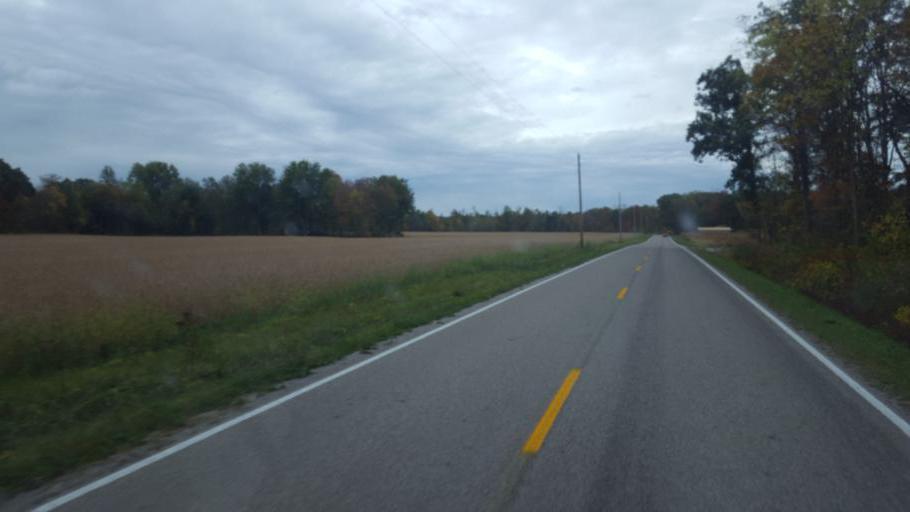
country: US
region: Ohio
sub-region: Huron County
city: New London
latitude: 41.1695
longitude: -82.4446
